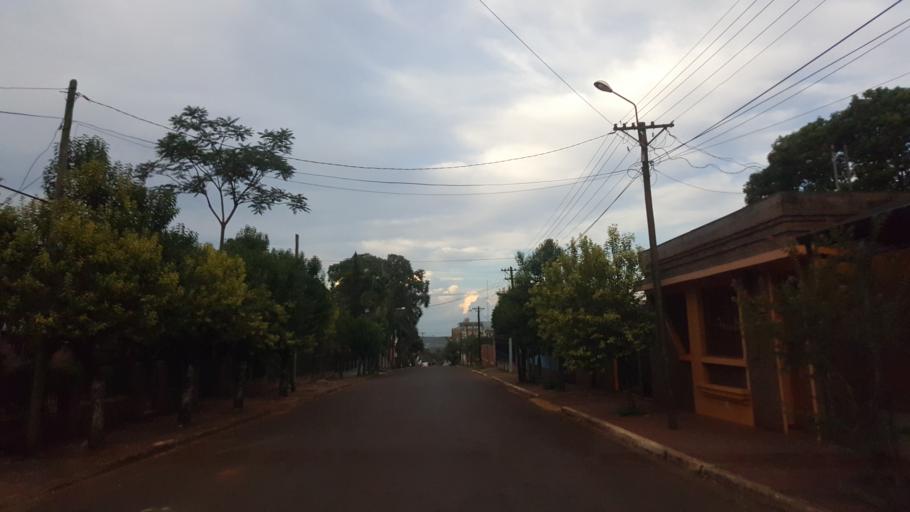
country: AR
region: Misiones
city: Jardin America
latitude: -27.0458
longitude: -55.2316
